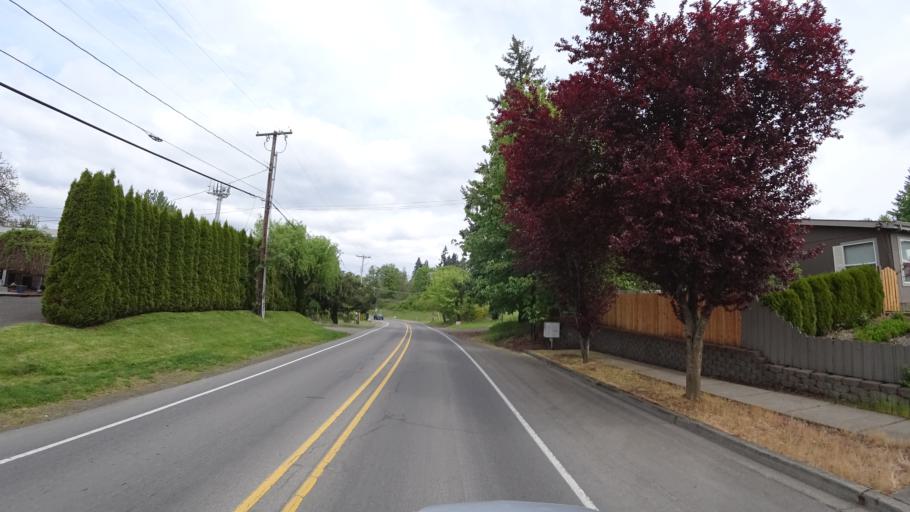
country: US
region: Oregon
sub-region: Washington County
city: Hillsboro
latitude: 45.5339
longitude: -122.9930
